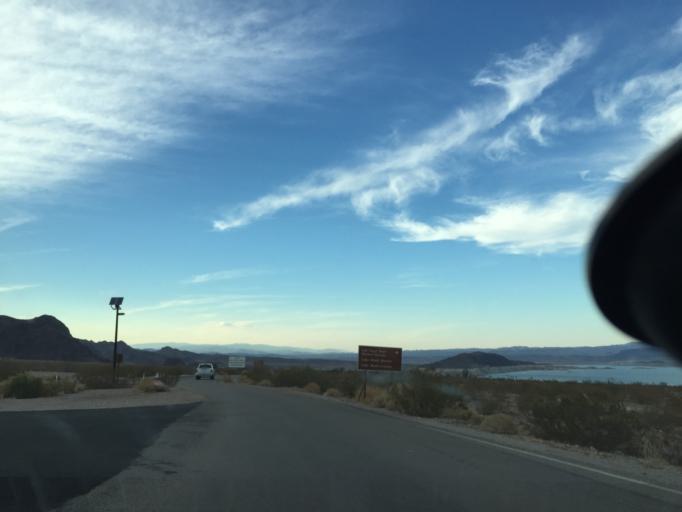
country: US
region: Nevada
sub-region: Clark County
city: Boulder City
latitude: 36.0211
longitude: -114.7961
